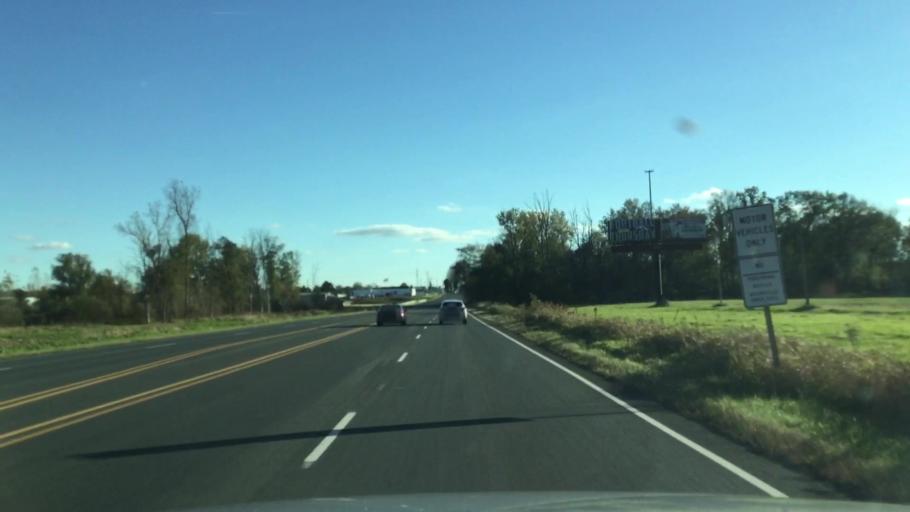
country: US
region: Michigan
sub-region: Kalamazoo County
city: Eastwood
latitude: 42.2766
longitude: -85.5308
